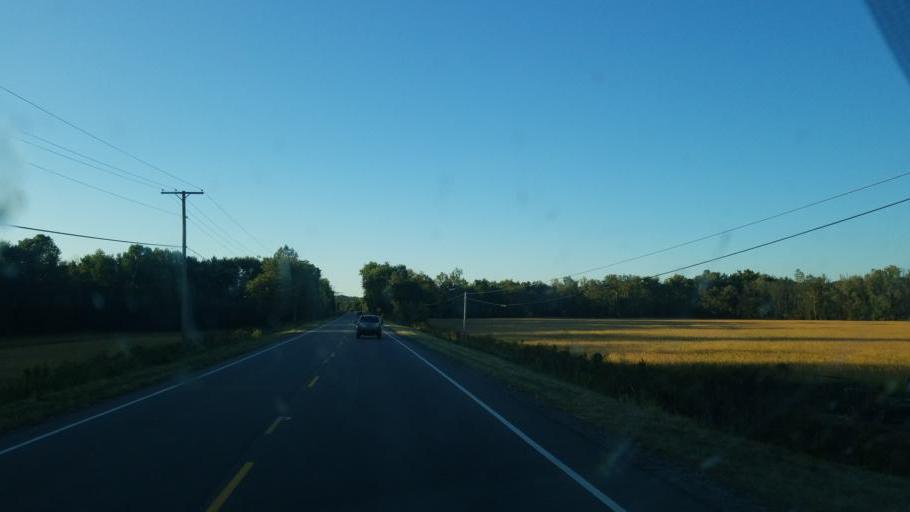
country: US
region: Ohio
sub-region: Coshocton County
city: Coshocton
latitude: 40.3233
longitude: -81.9394
